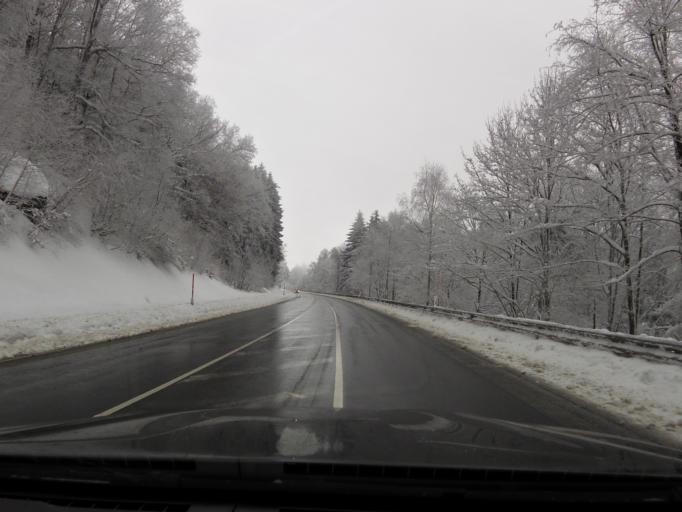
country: DE
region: Bavaria
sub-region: Lower Bavaria
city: Schofweg
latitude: 48.8499
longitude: 13.2048
